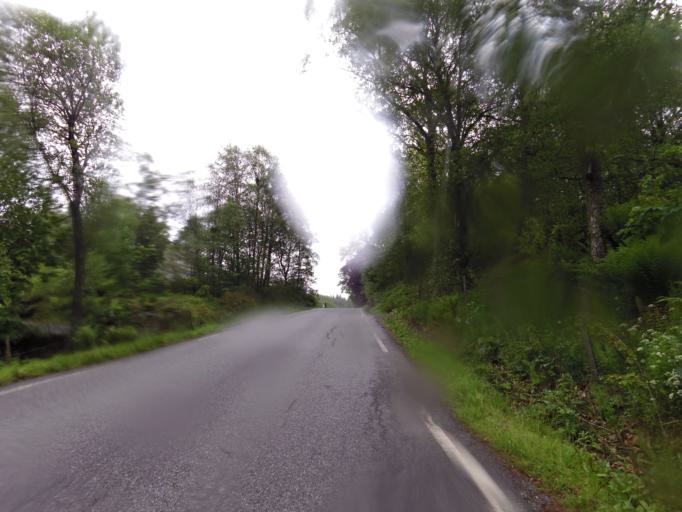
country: NO
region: Hordaland
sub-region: Sveio
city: Sveio
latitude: 59.5262
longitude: 5.2804
